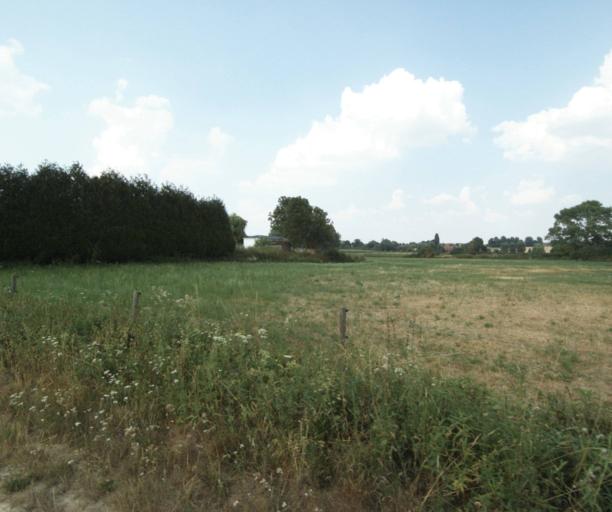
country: FR
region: Nord-Pas-de-Calais
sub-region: Departement du Nord
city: Linselles
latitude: 50.7268
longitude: 3.0810
